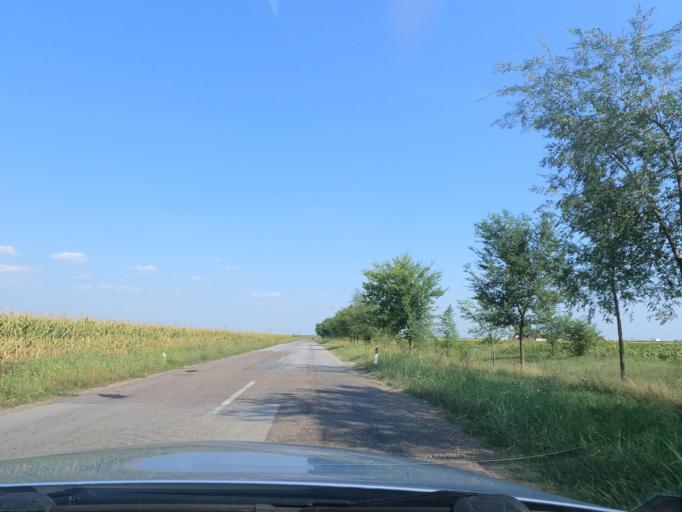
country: RS
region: Autonomna Pokrajina Vojvodina
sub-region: Juznobacki Okrug
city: Becej
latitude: 45.6520
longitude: 19.9711
